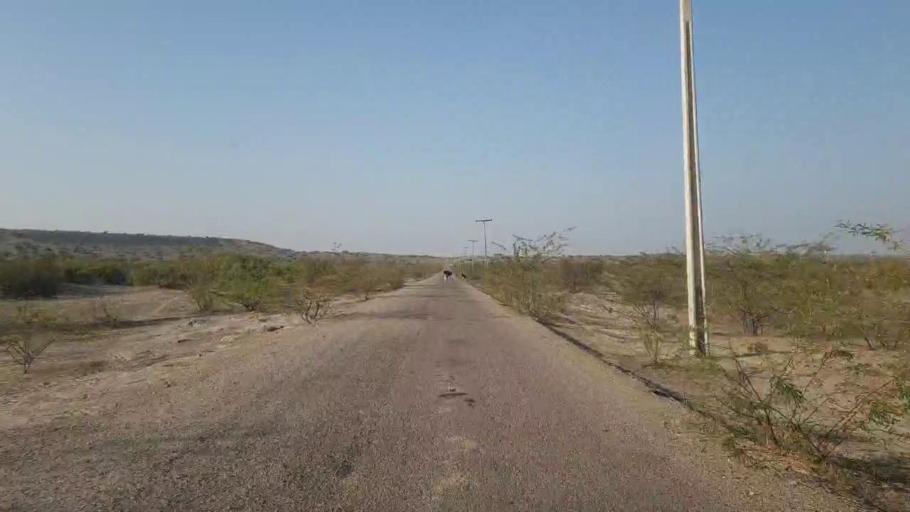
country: PK
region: Sindh
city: Chor
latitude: 25.5975
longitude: 69.8380
